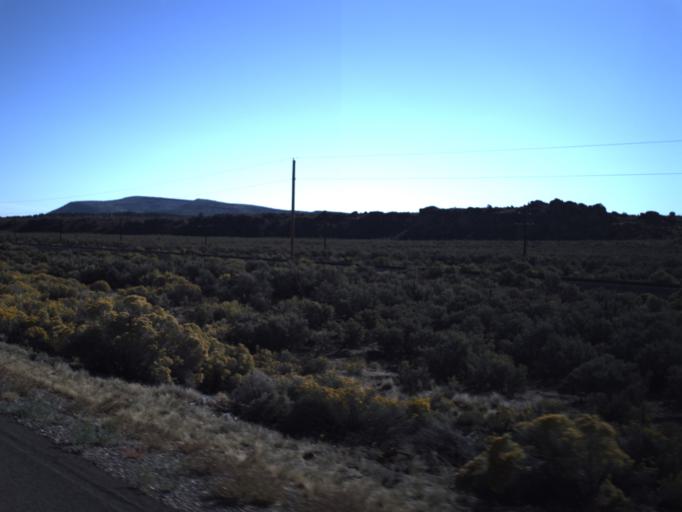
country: US
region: Utah
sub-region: Washington County
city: Enterprise
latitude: 37.7395
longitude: -114.0159
